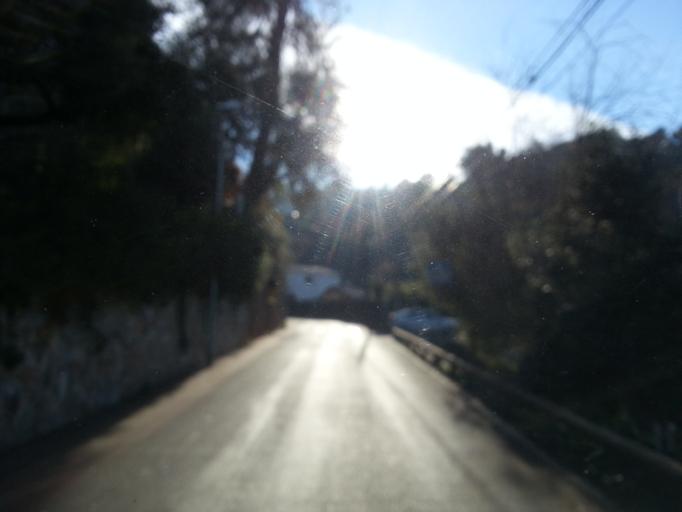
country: ES
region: Catalonia
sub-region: Provincia de Barcelona
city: Sant Cugat del Valles
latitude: 41.4261
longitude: 2.0899
